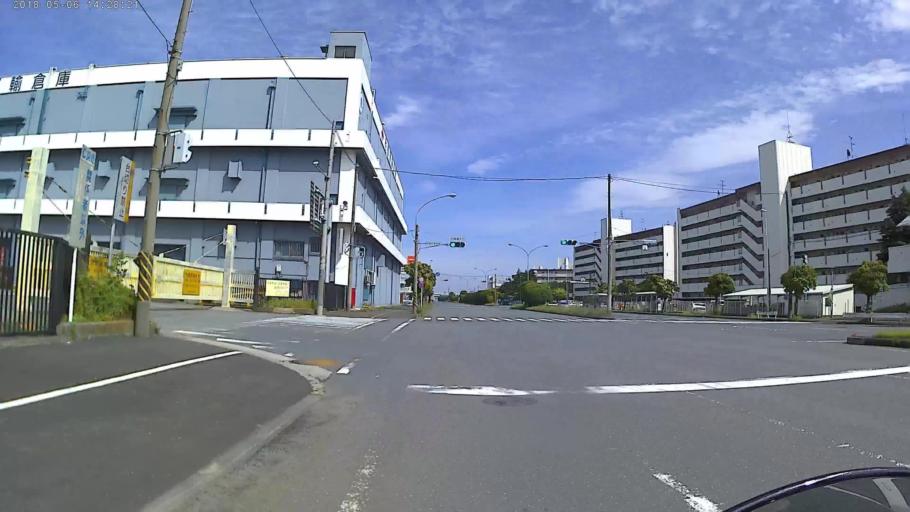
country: JP
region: Kanagawa
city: Yokohama
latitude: 35.4304
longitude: 139.6732
